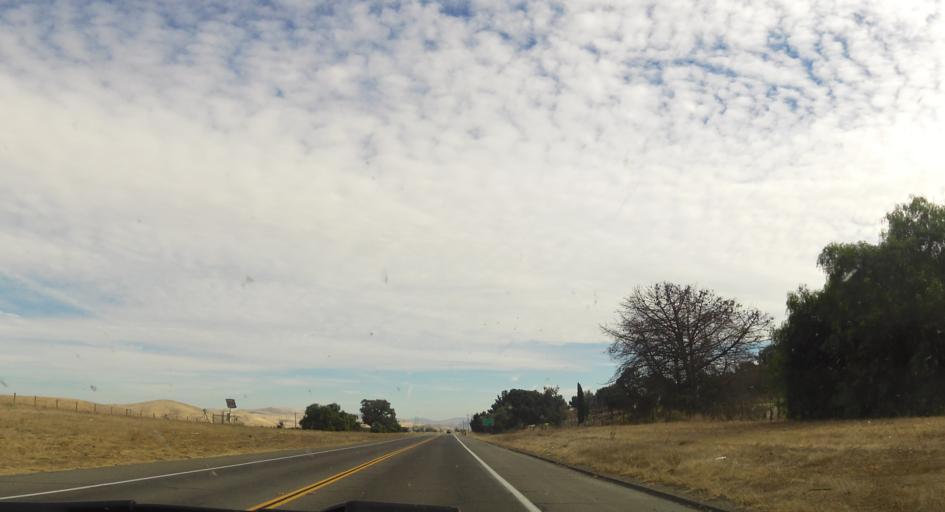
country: US
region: California
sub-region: San Benito County
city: Ridgemark
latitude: 36.8119
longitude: -121.3489
